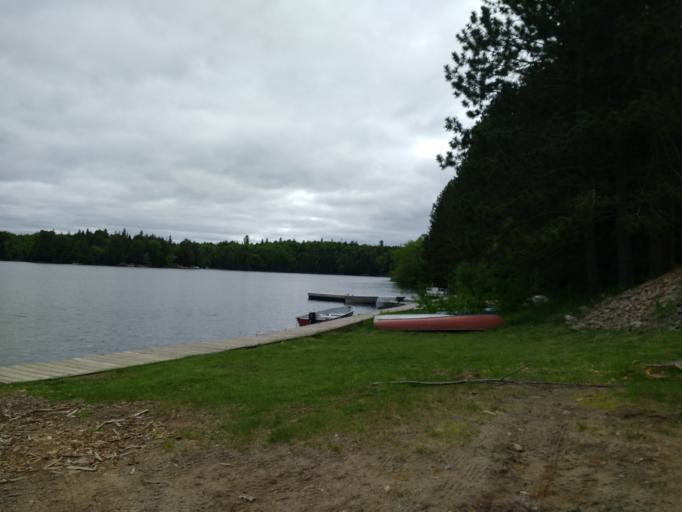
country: CA
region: Ontario
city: Huntsville
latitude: 45.5520
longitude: -78.5934
